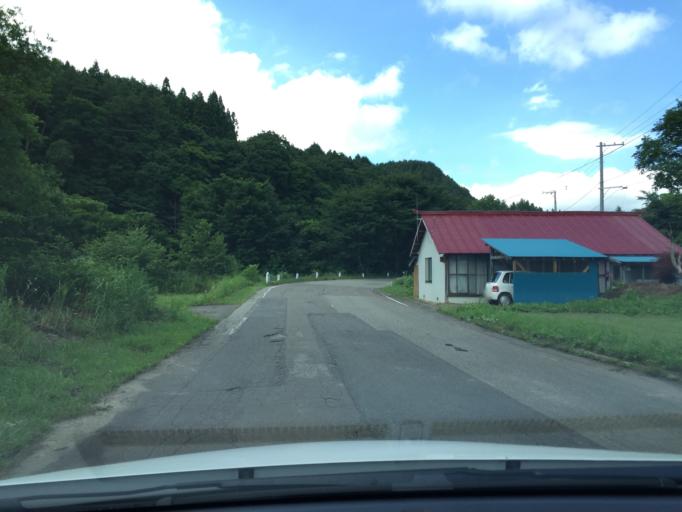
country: JP
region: Fukushima
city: Inawashiro
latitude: 37.2826
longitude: 140.0619
